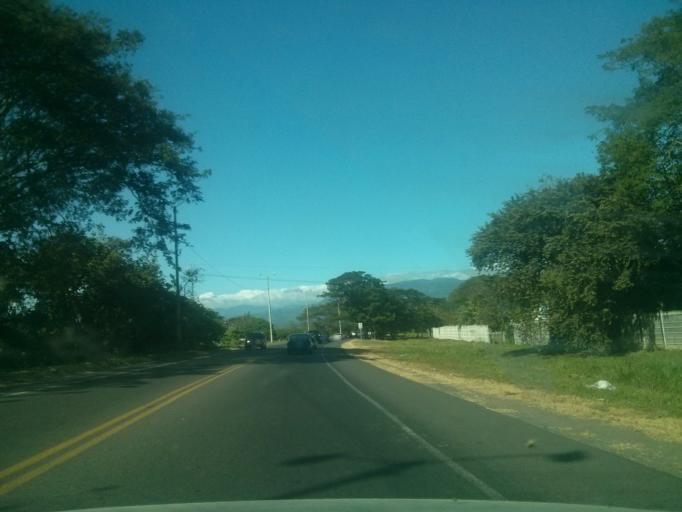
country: CR
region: Puntarenas
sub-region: Canton Central de Puntarenas
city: Chacarita
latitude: 9.9815
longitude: -84.7399
